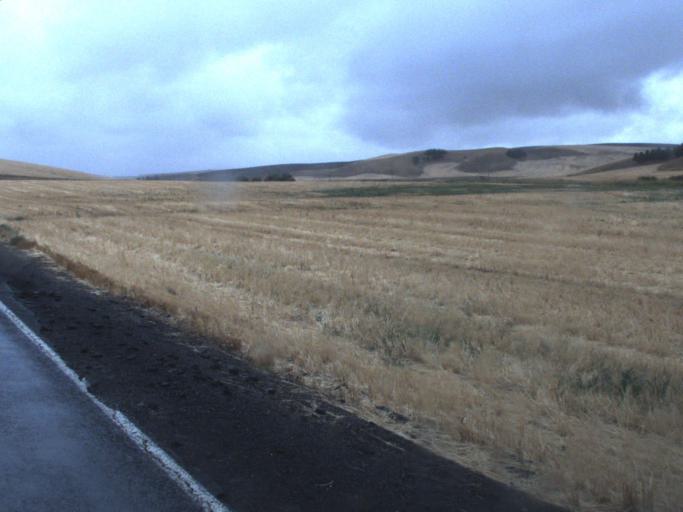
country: US
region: Washington
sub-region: Spokane County
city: Cheney
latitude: 47.1620
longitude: -117.8708
